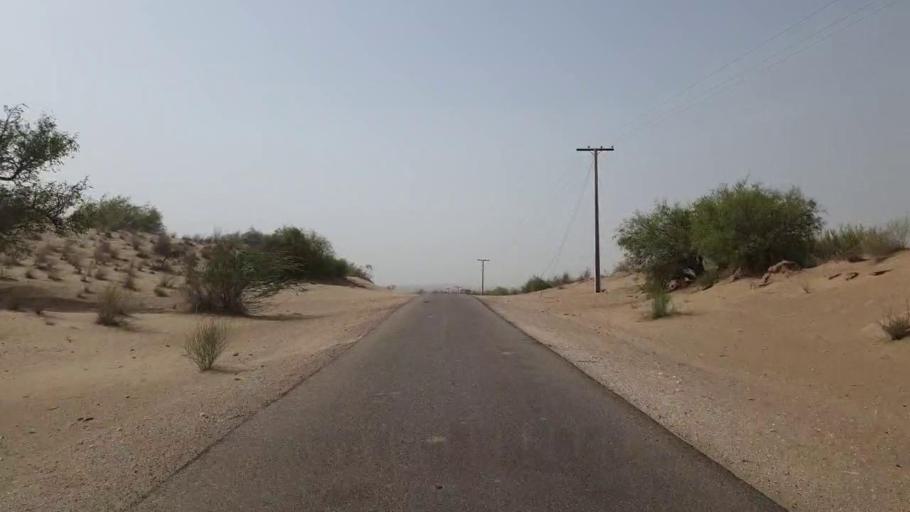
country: PK
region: Sindh
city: Mithi
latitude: 24.5992
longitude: 69.9242
